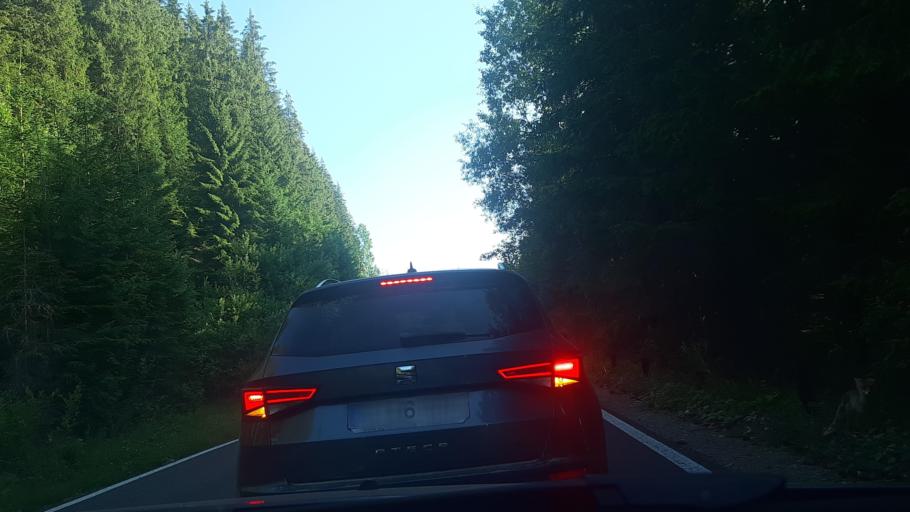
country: RO
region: Alba
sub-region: Comuna Sugag
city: Sugag
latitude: 45.5723
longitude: 23.6212
